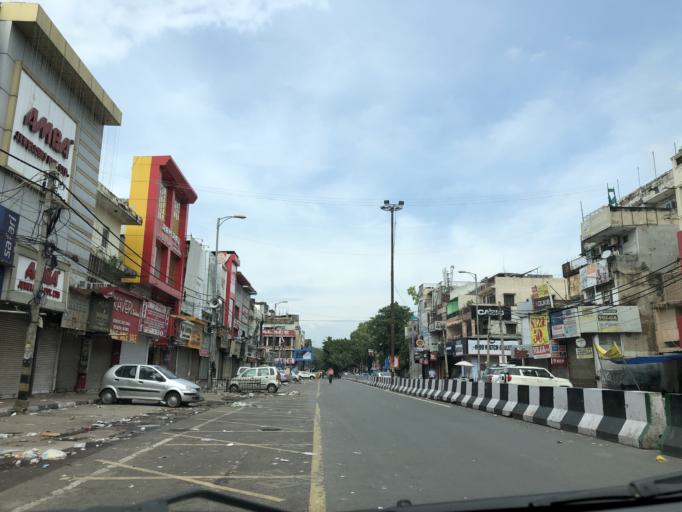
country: IN
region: NCT
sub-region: New Delhi
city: New Delhi
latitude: 28.5695
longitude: 77.2426
